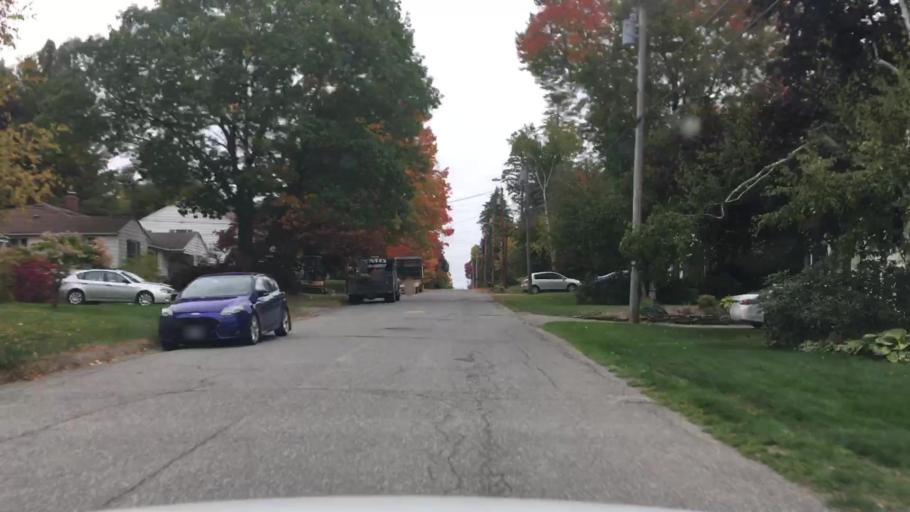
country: US
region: Maine
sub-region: Kennebec County
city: Waterville
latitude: 44.5625
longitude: -69.6418
